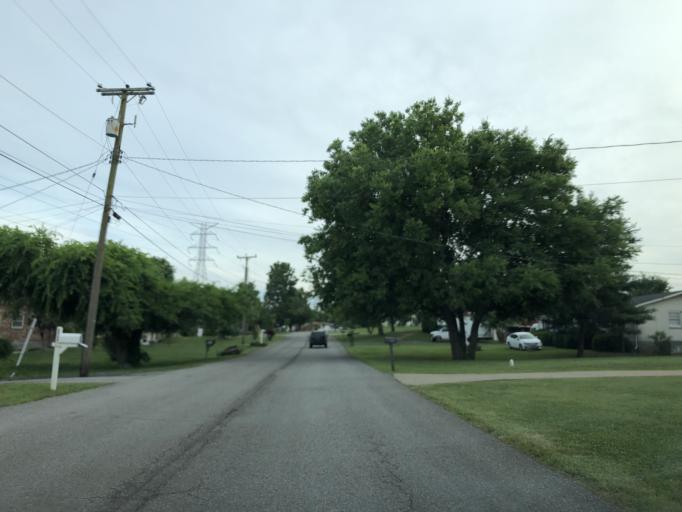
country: US
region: Tennessee
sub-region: Davidson County
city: Goodlettsville
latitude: 36.2960
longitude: -86.7133
